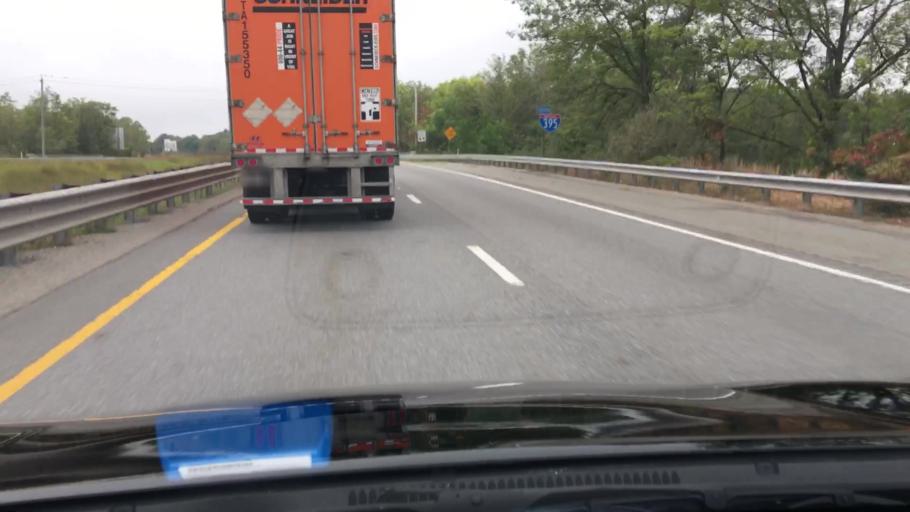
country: US
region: Massachusetts
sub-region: Worcester County
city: Webster
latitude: 42.0552
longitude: -71.8620
